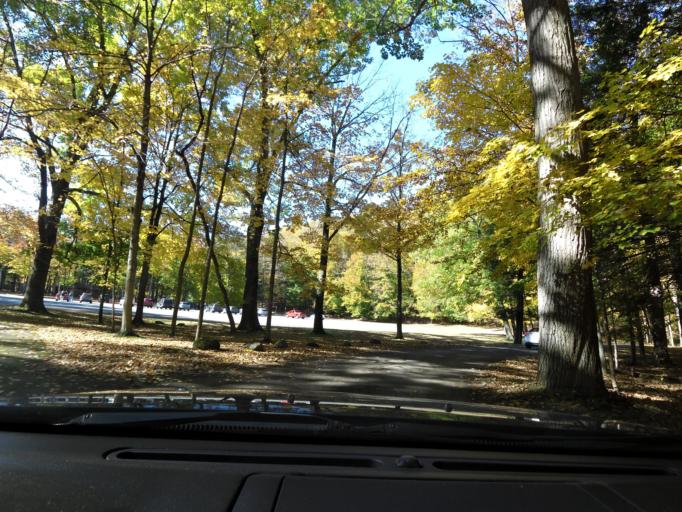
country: US
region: New York
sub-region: Wyoming County
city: Castile
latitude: 42.5886
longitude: -78.0151
